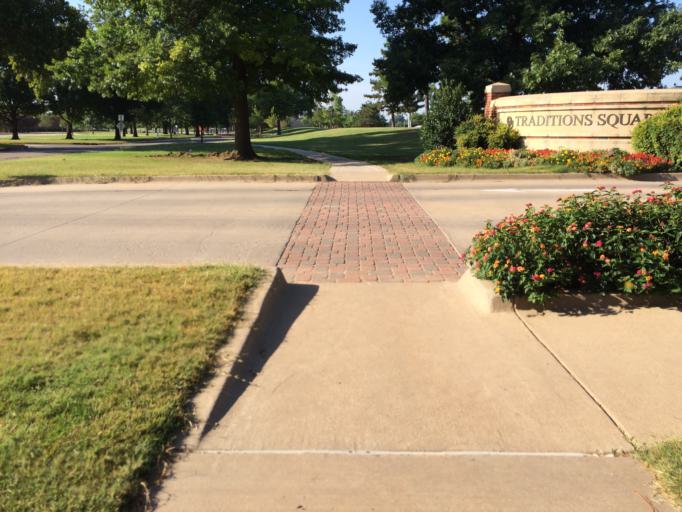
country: US
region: Oklahoma
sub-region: Cleveland County
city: Norman
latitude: 35.1921
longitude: -97.4452
